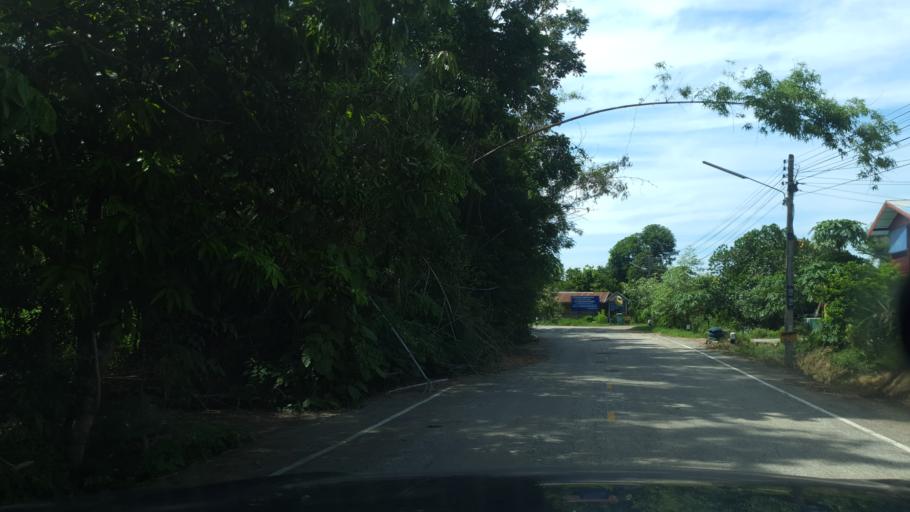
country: TH
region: Sukhothai
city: Si Samrong
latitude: 17.1990
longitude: 99.7228
